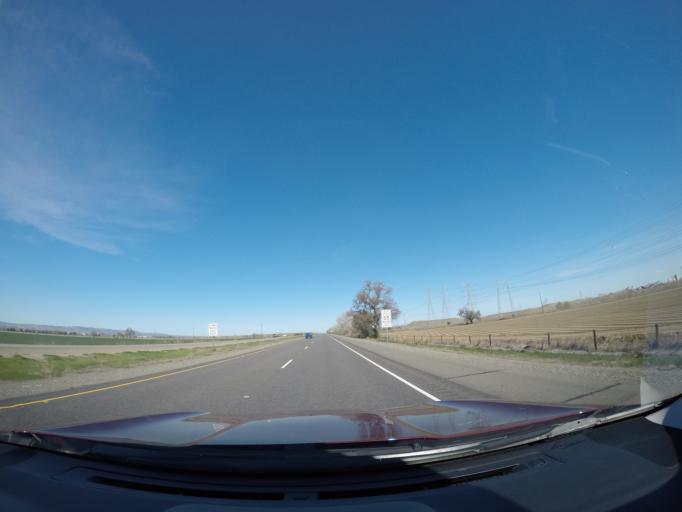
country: US
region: California
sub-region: Yolo County
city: Cottonwood
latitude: 38.6888
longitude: -121.9529
